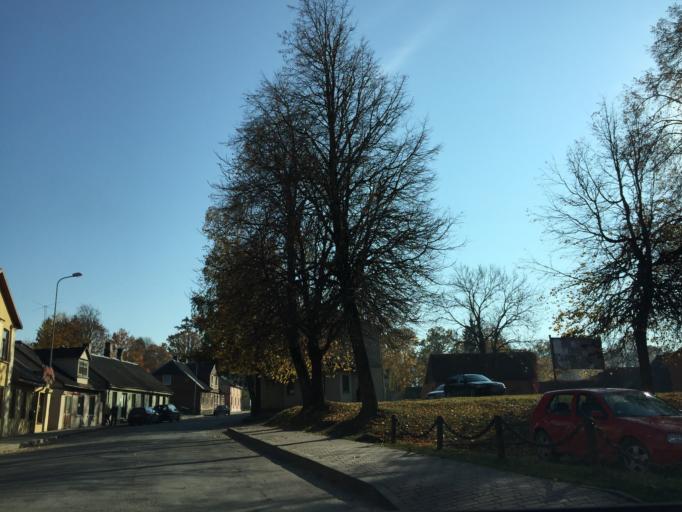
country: LV
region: Saldus Rajons
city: Saldus
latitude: 56.6643
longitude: 22.4955
